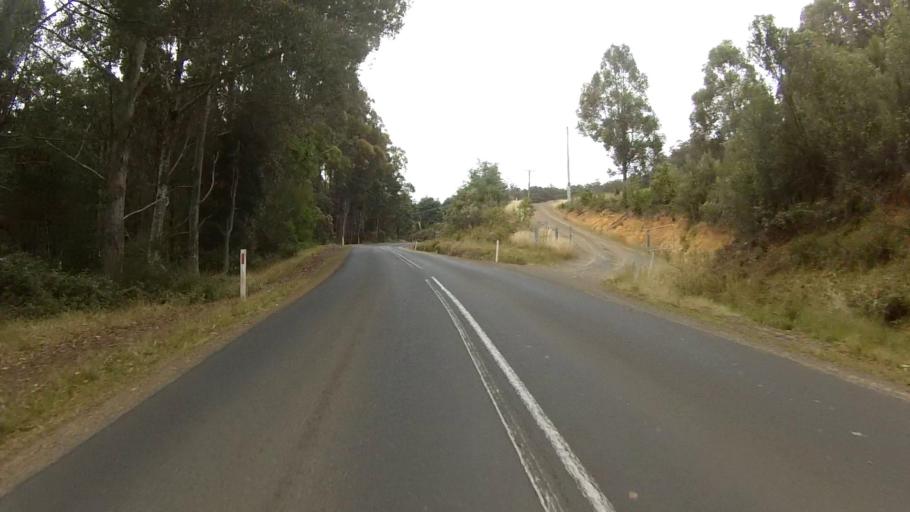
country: AU
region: Tasmania
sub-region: Huon Valley
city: Cygnet
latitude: -43.1475
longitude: 147.1530
